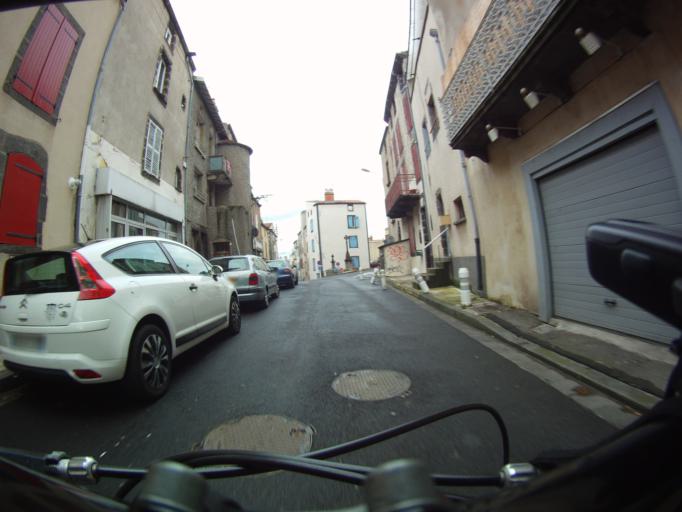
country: FR
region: Auvergne
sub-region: Departement du Puy-de-Dome
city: Beaumont
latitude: 45.7508
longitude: 3.0854
